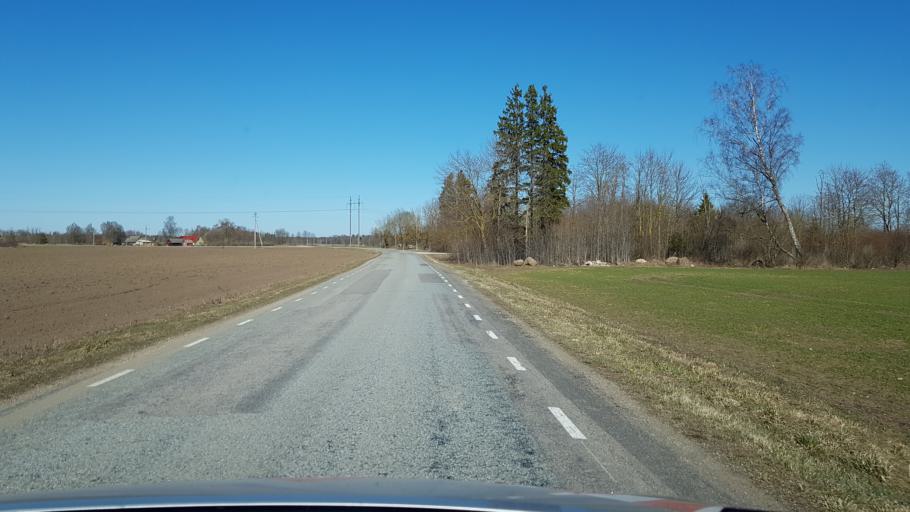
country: EE
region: Laeaene-Virumaa
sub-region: Someru vald
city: Someru
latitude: 59.3720
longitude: 26.4512
